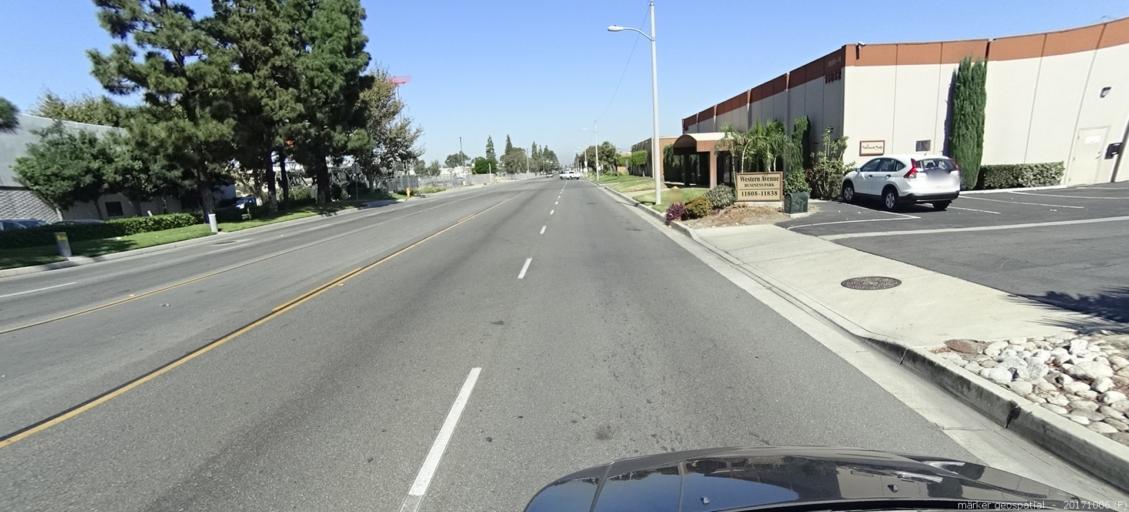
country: US
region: California
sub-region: Orange County
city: Stanton
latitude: 33.7905
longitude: -118.0015
